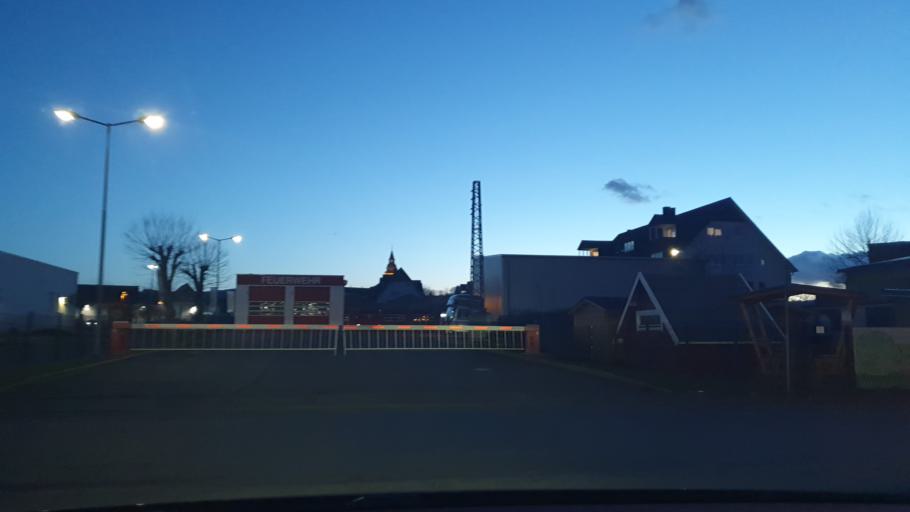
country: DE
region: Hesse
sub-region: Regierungsbezirk Giessen
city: Haiger
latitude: 50.7441
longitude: 8.2083
